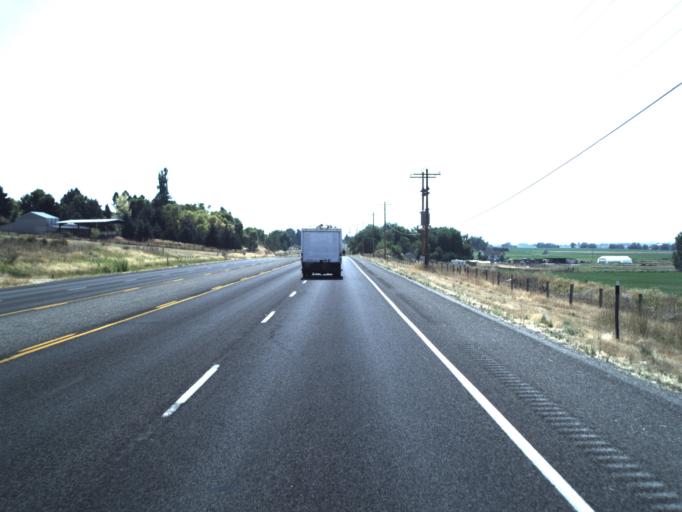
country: US
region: Utah
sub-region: Cache County
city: Richmond
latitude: 41.8845
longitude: -111.8187
